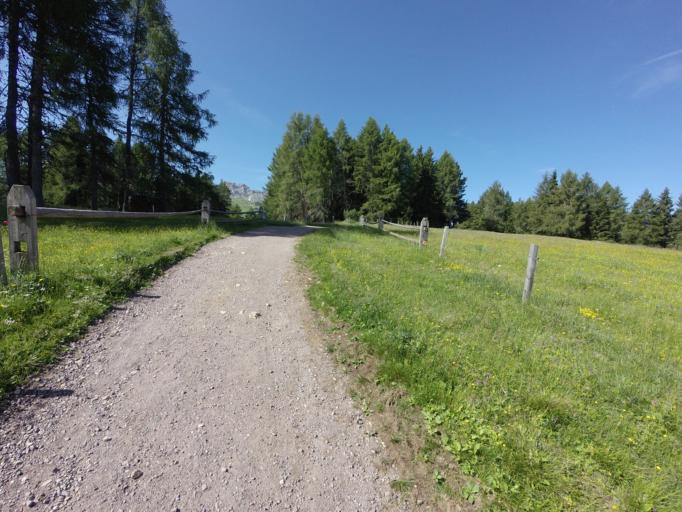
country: IT
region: Trentino-Alto Adige
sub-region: Bolzano
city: Ortisei
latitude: 46.5363
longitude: 11.6451
